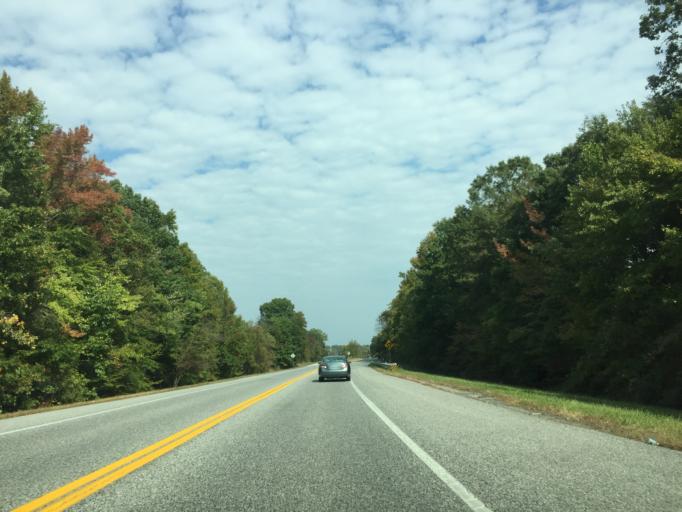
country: US
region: Maryland
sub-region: Harford County
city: Edgewood
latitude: 39.4288
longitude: -76.3092
